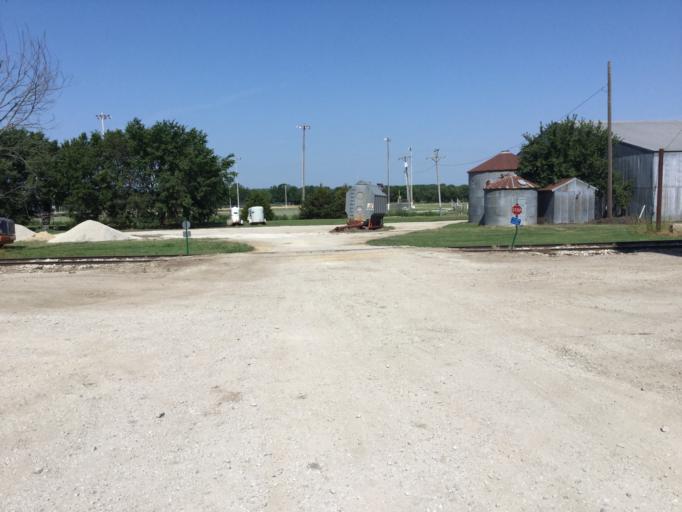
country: US
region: Kansas
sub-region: Montgomery County
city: Caney
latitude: 37.0114
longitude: -95.9419
